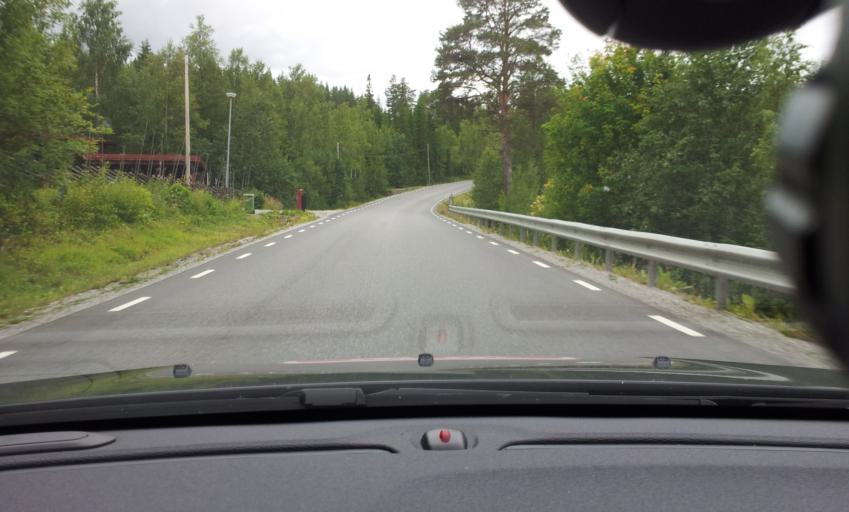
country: SE
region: Jaemtland
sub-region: Braecke Kommun
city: Braecke
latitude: 62.9621
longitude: 15.1741
